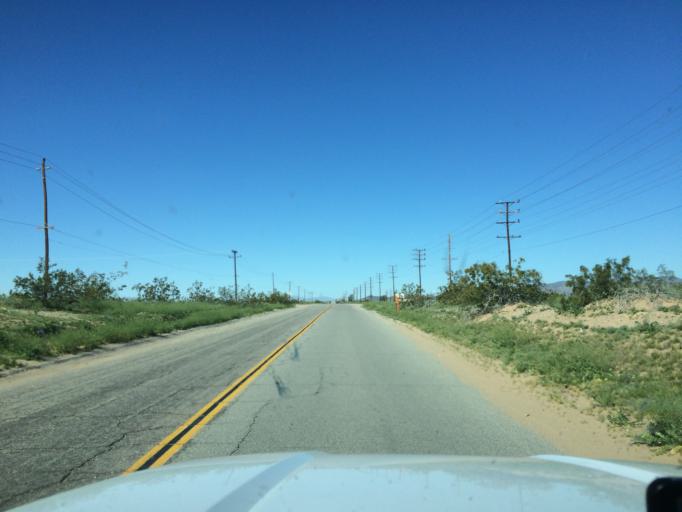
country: US
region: California
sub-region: Riverside County
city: Mesa Verde
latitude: 33.6102
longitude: -114.6732
